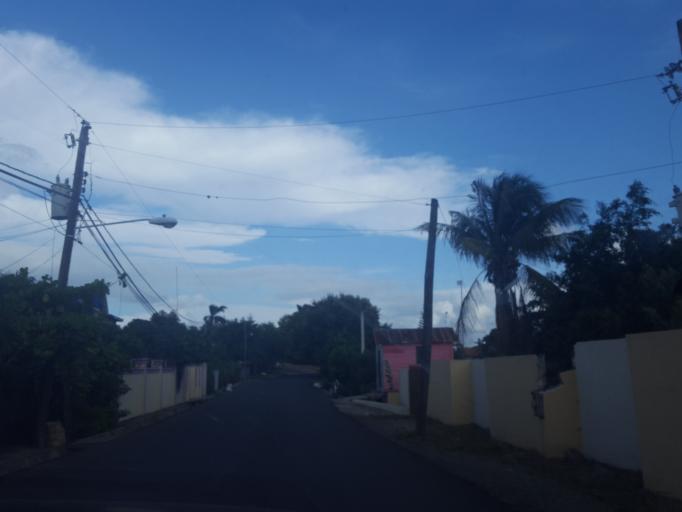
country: DO
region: La Vega
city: Rio Verde Arriba
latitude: 19.3510
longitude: -70.6274
